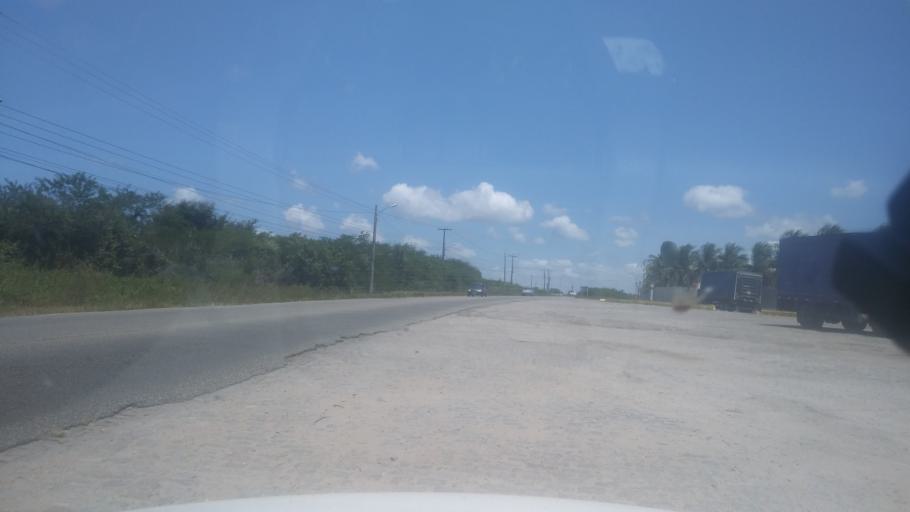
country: BR
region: Rio Grande do Norte
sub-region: Extremoz
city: Extremoz
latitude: -5.7189
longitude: -35.2774
